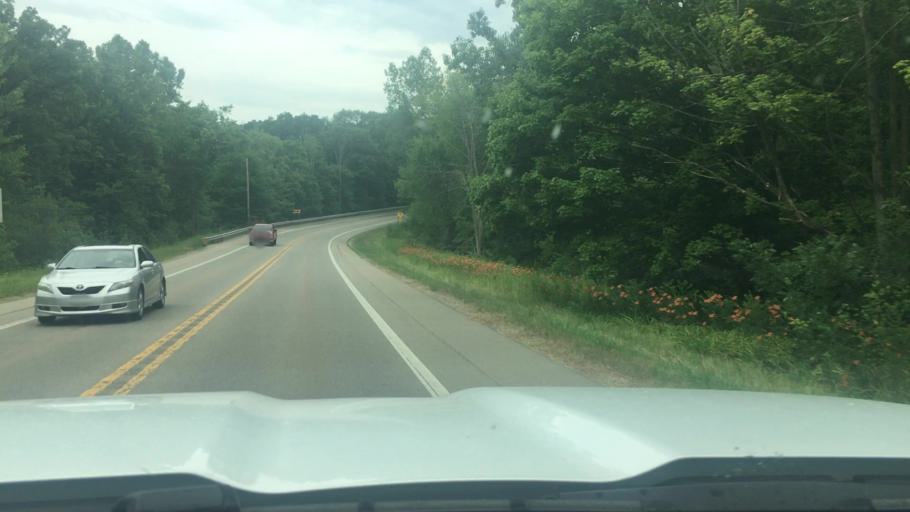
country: US
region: Michigan
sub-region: Ionia County
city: Ionia
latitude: 42.9745
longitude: -85.1235
